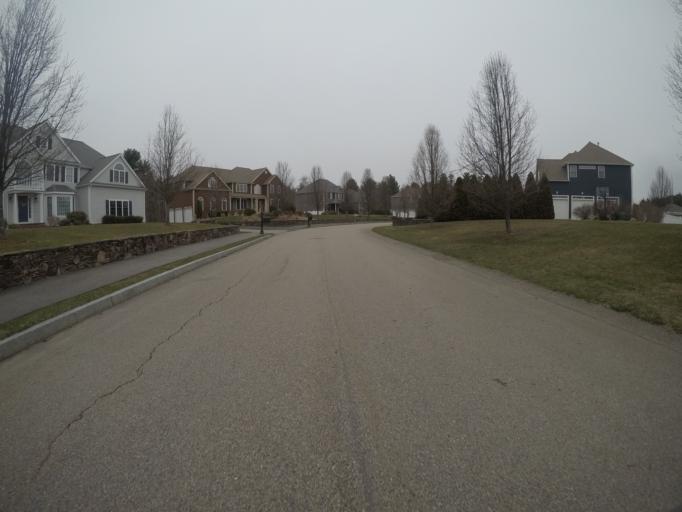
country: US
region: Massachusetts
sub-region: Bristol County
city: Easton
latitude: 42.0145
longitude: -71.1102
